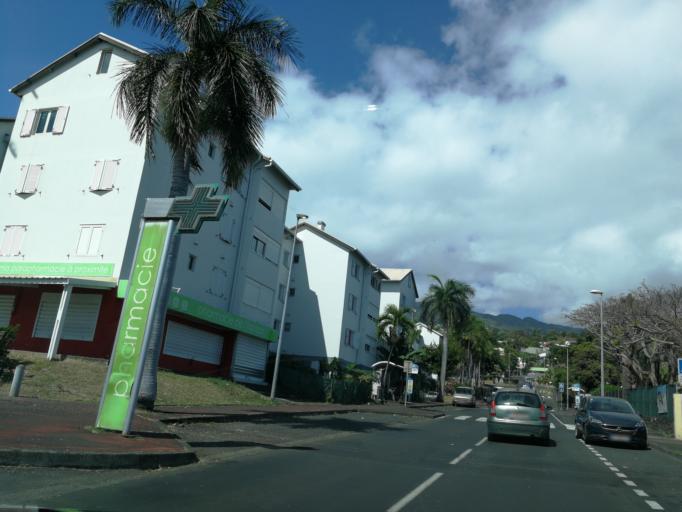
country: RE
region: Reunion
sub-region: Reunion
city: Saint-Denis
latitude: -20.9088
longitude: 55.4828
